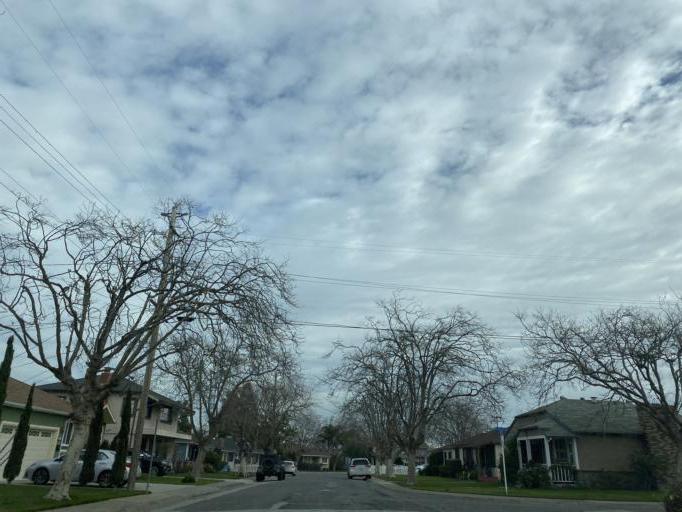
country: US
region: California
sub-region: San Mateo County
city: Millbrae
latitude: 37.6049
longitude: -122.3900
